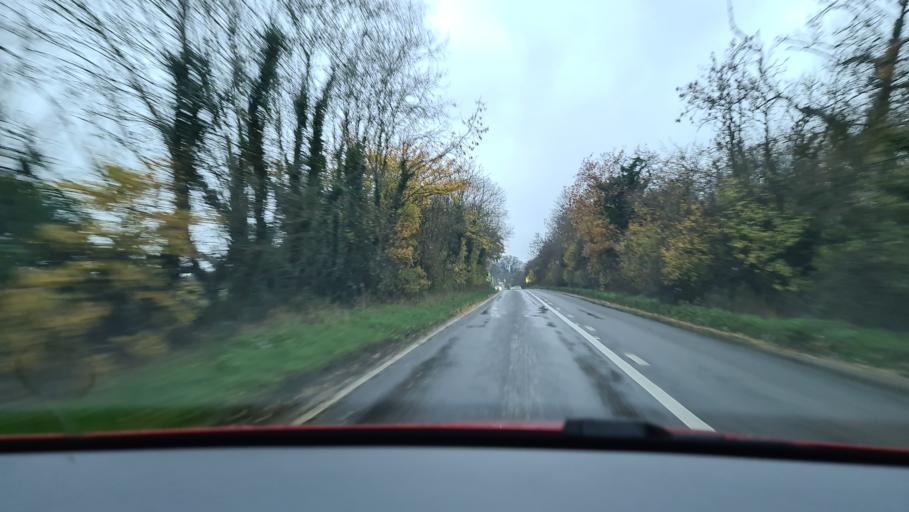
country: GB
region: England
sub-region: Oxfordshire
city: Somerton
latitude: 51.9459
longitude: -1.2093
